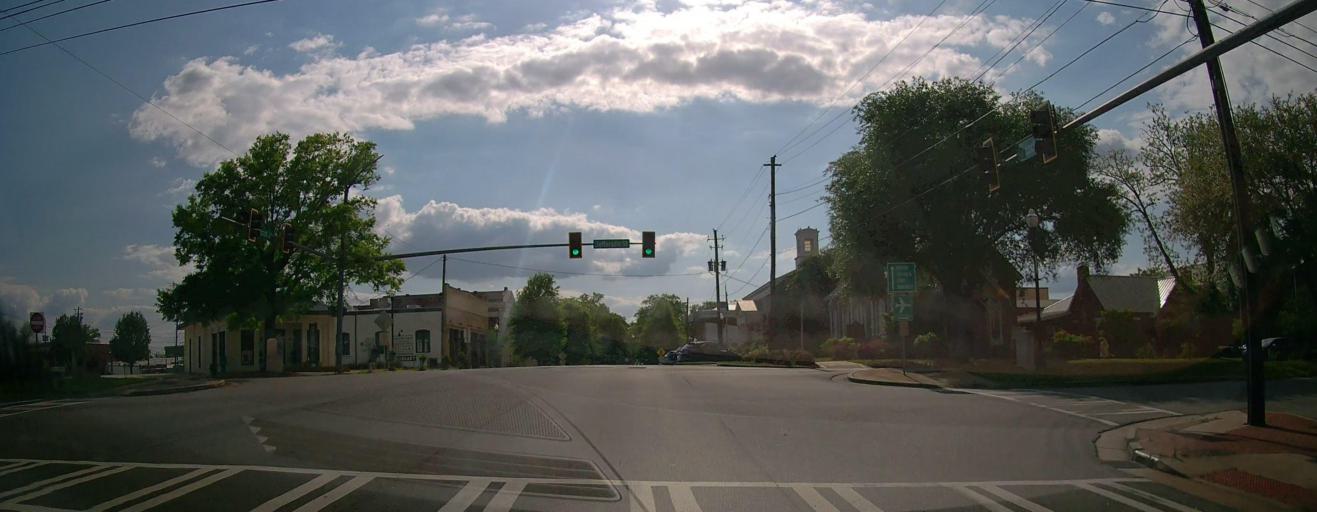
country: US
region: Georgia
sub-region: Baldwin County
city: Milledgeville
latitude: 33.0817
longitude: -83.2252
